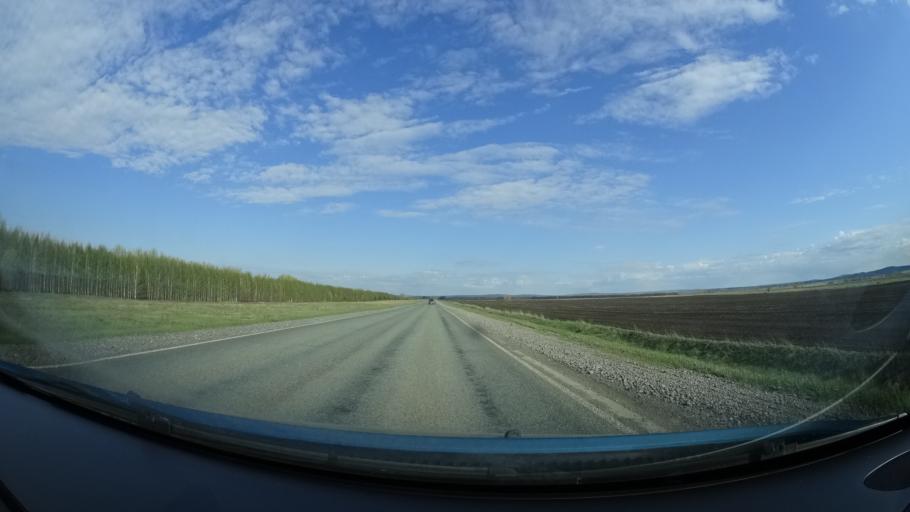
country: RU
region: Bashkortostan
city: Blagoveshchensk
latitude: 55.2007
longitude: 55.8264
